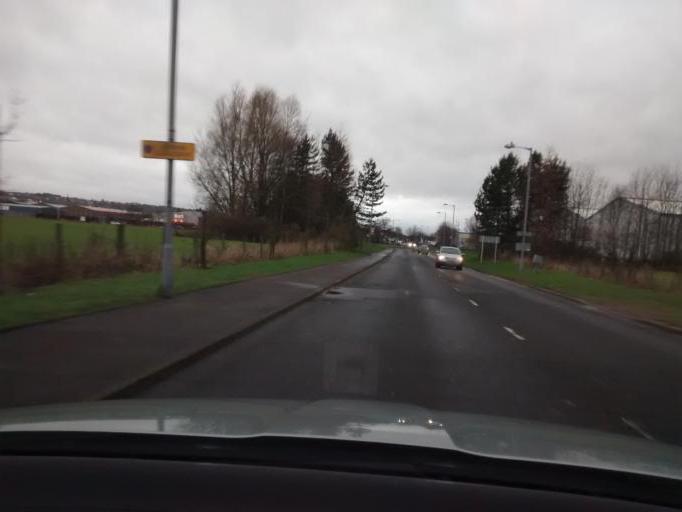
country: GB
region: Scotland
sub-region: Falkirk
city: Falkirk
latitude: 56.0118
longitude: -3.7621
